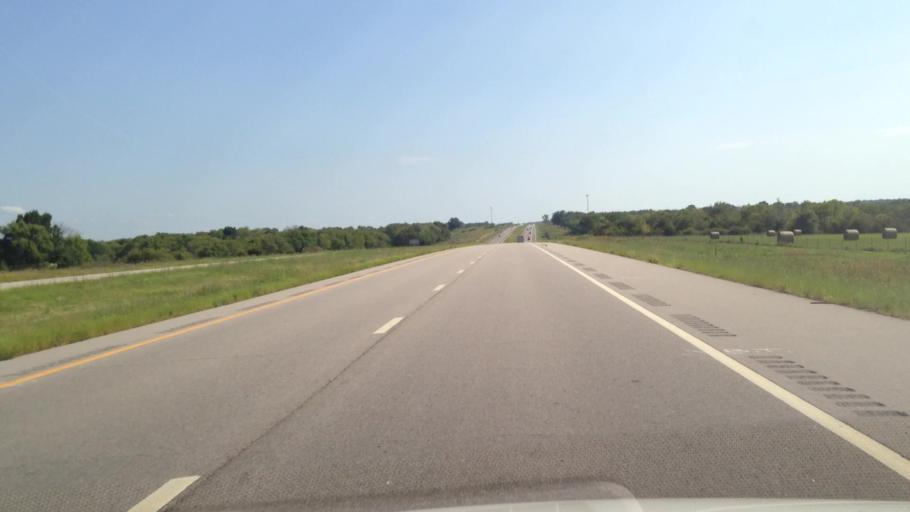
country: US
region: Kansas
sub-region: Linn County
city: La Cygne
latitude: 38.3938
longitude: -94.6878
